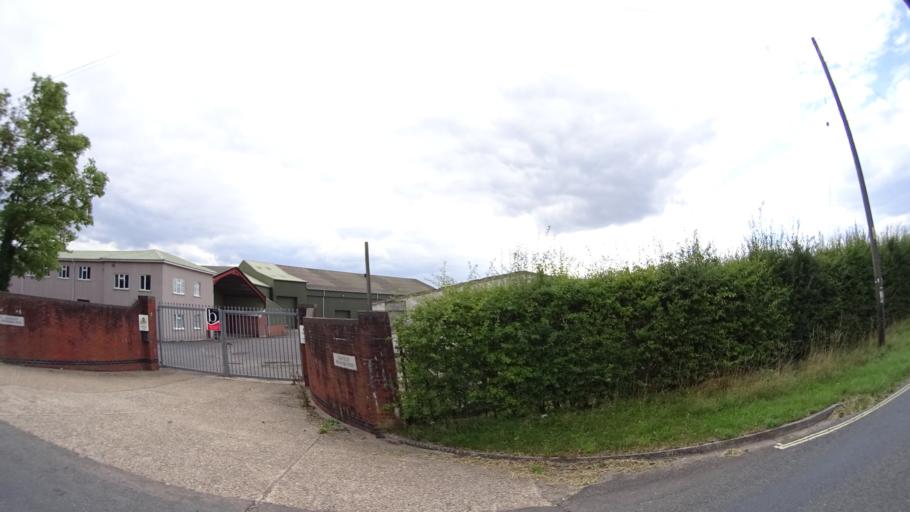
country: GB
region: England
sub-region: Wiltshire
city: Tidworth
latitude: 51.1712
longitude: -1.6260
